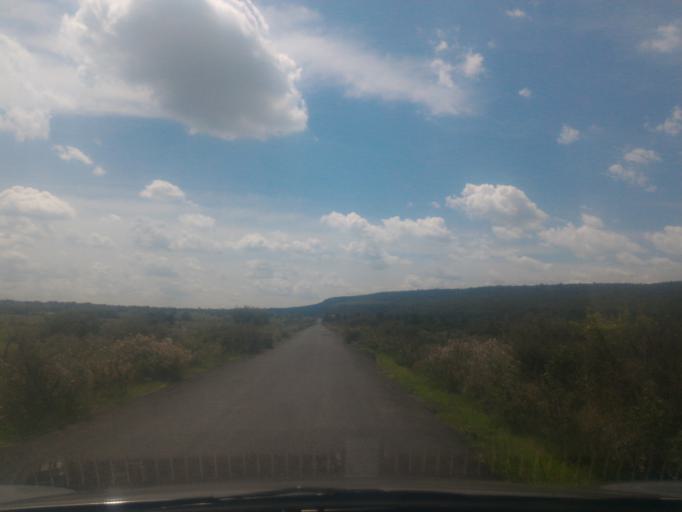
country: MX
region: Guanajuato
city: Ciudad Manuel Doblado
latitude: 20.8397
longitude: -102.0446
